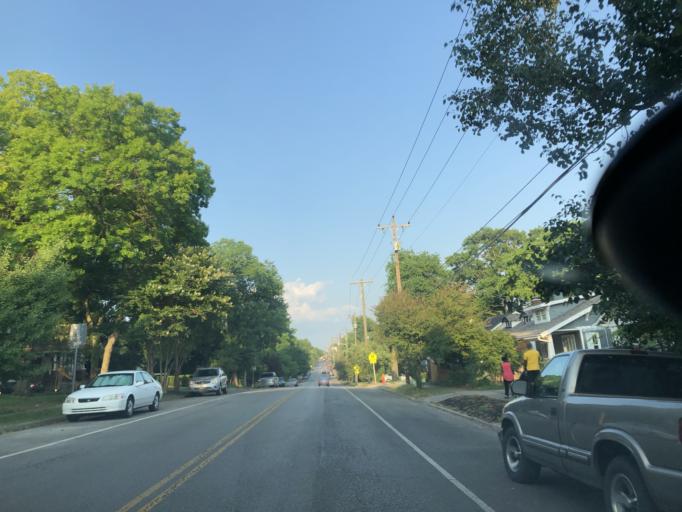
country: US
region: Tennessee
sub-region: Davidson County
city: Nashville
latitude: 36.1312
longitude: -86.8092
